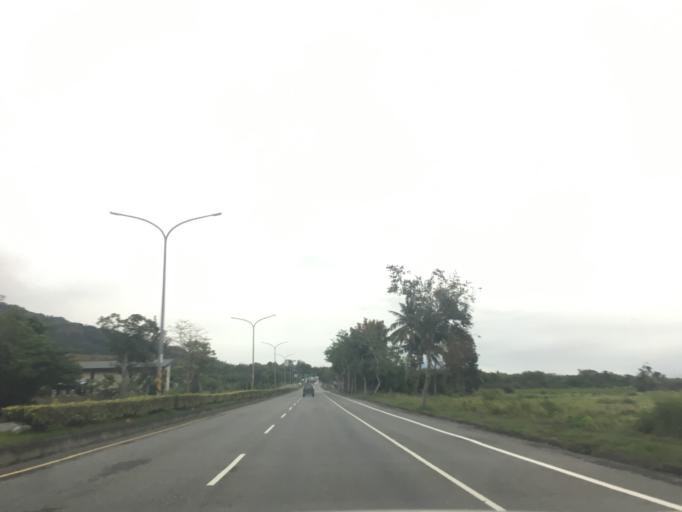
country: TW
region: Taiwan
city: Taitung City
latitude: 22.7093
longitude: 121.0434
